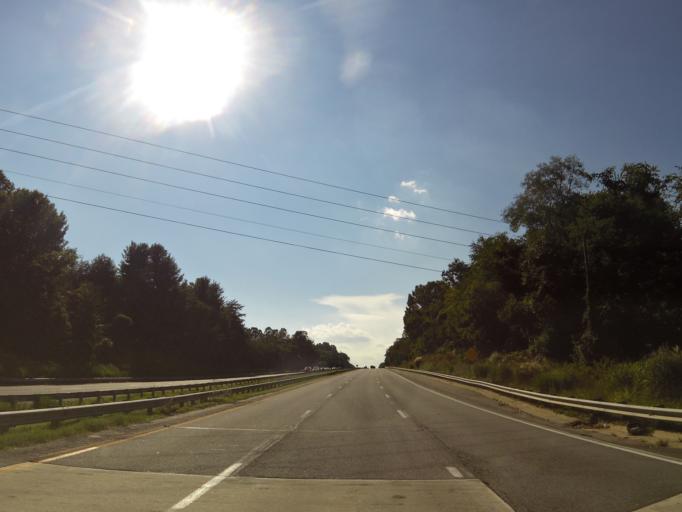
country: US
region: North Carolina
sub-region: Buncombe County
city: Biltmore Forest
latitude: 35.5567
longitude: -82.5222
